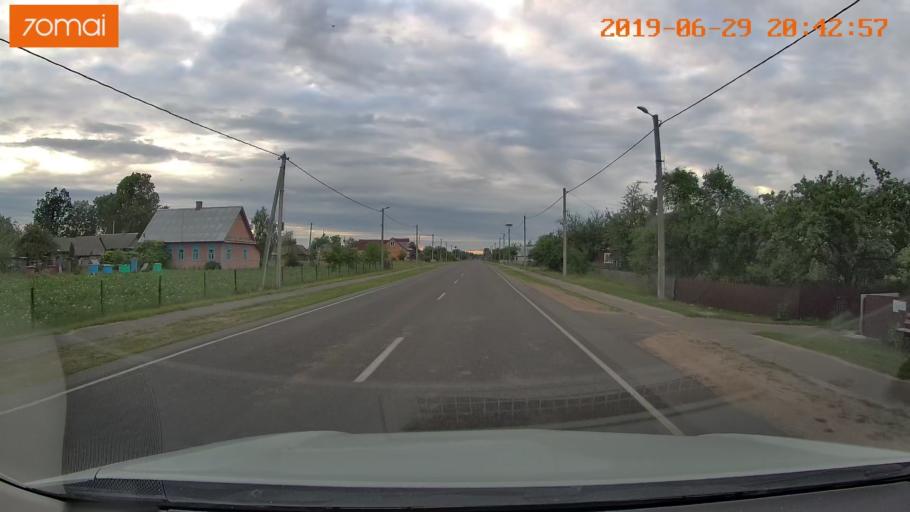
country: BY
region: Brest
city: Hantsavichy
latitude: 52.6016
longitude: 26.3206
